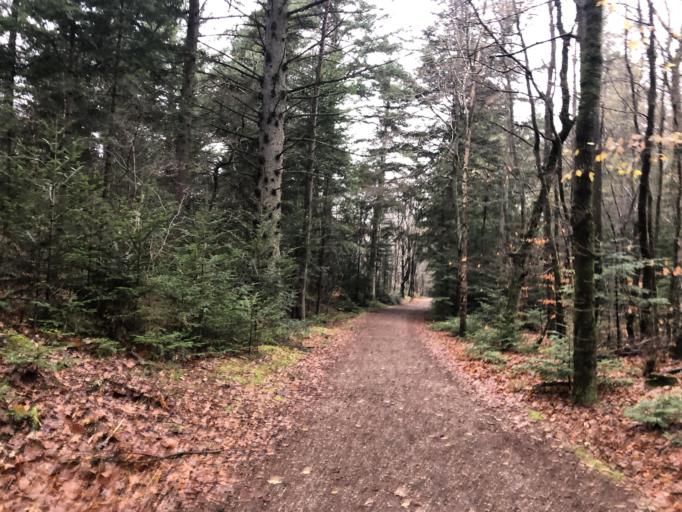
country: DK
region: Central Jutland
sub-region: Holstebro Kommune
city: Ulfborg
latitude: 56.2879
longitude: 8.1684
